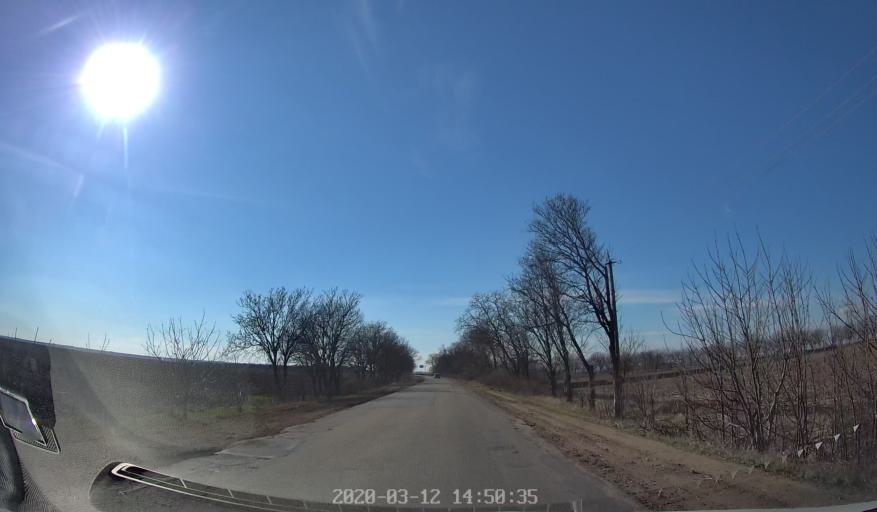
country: MD
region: Criuleni
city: Criuleni
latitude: 47.2230
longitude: 29.1271
